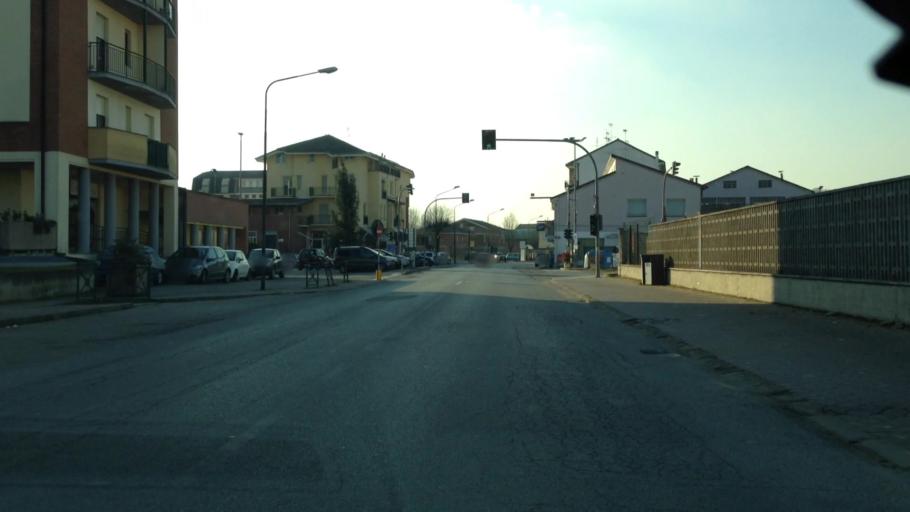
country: IT
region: Piedmont
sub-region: Provincia di Asti
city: Mombercelli
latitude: 44.8232
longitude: 8.2948
